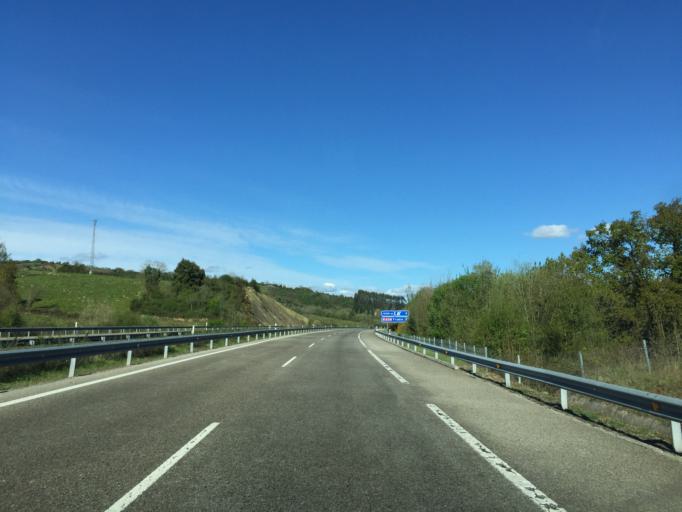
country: ES
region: Asturias
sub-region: Province of Asturias
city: Castandiello
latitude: 43.3537
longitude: -5.9338
